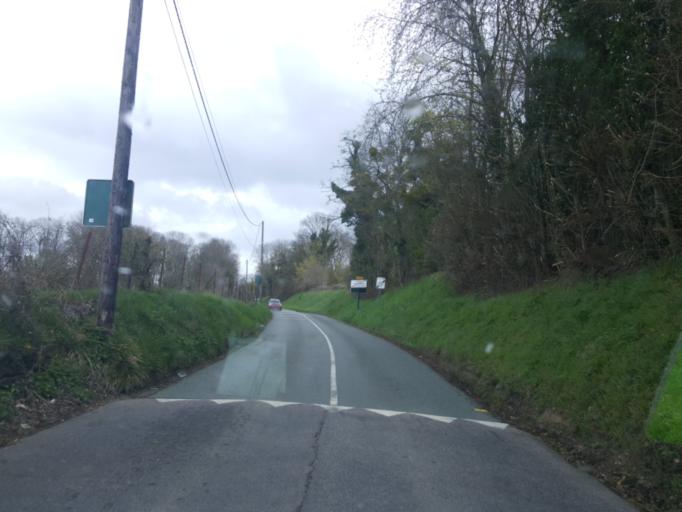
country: FR
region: Ile-de-France
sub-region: Departement du Val-d'Oise
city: Magny-en-Vexin
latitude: 49.1651
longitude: 1.7816
